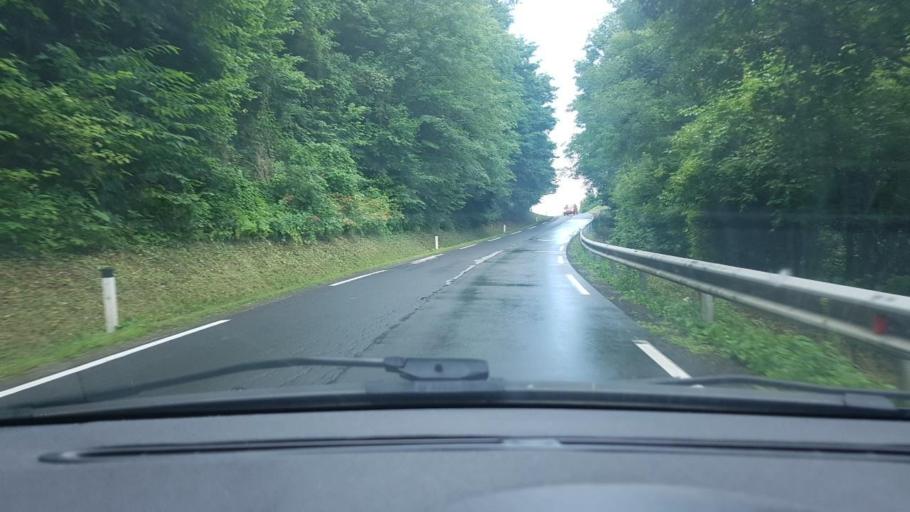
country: AT
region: Styria
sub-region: Politischer Bezirk Suedoststeiermark
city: Mureck
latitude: 46.6956
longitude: 15.7842
